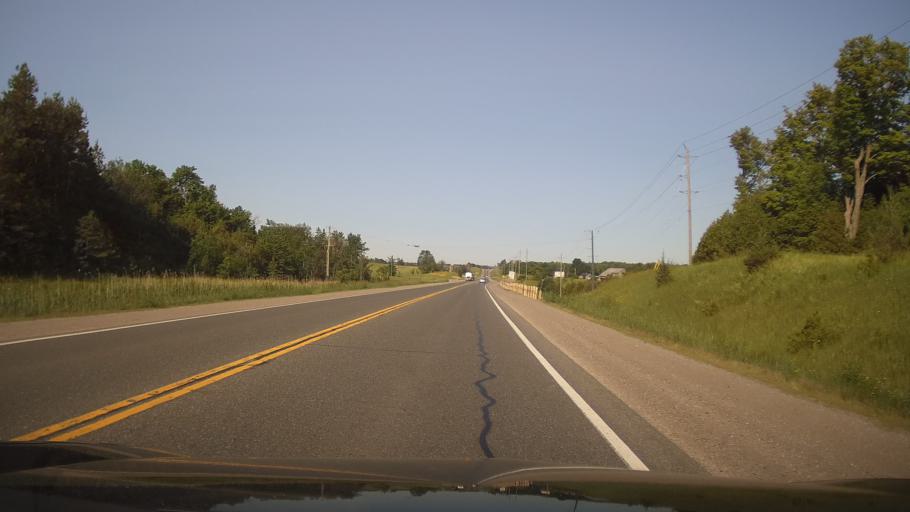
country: CA
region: Ontario
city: Peterborough
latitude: 44.3351
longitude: -78.1134
